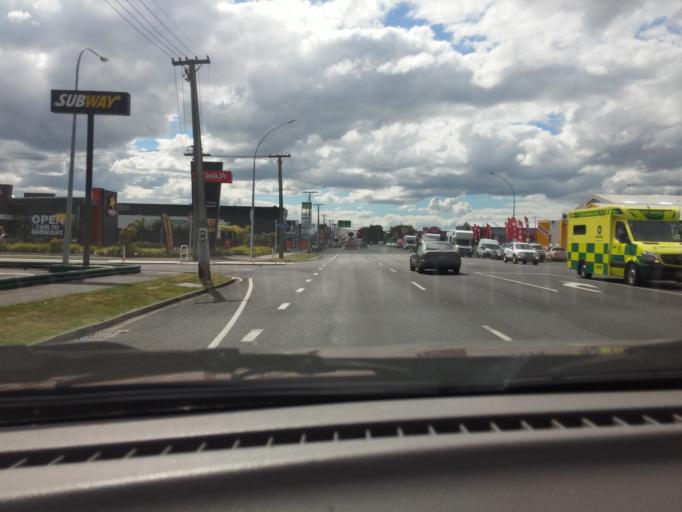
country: NZ
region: Waikato
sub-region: Hamilton City
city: Hamilton
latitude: -37.7922
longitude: 175.2602
